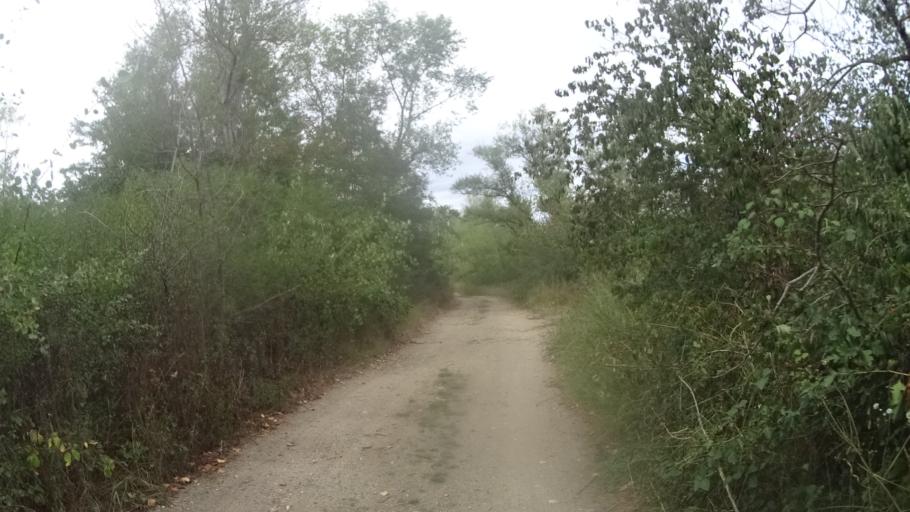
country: FR
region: Centre
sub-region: Departement du Cher
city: Cuffy
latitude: 46.9646
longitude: 3.0646
